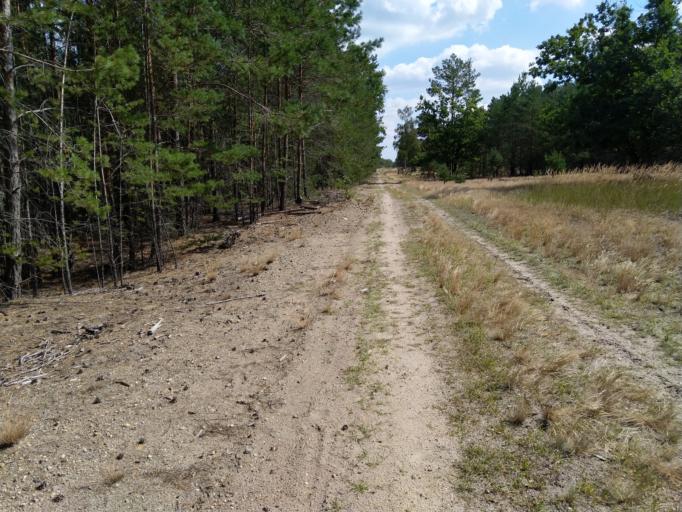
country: DE
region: Brandenburg
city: Luckenwalde
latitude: 52.0406
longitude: 13.1773
